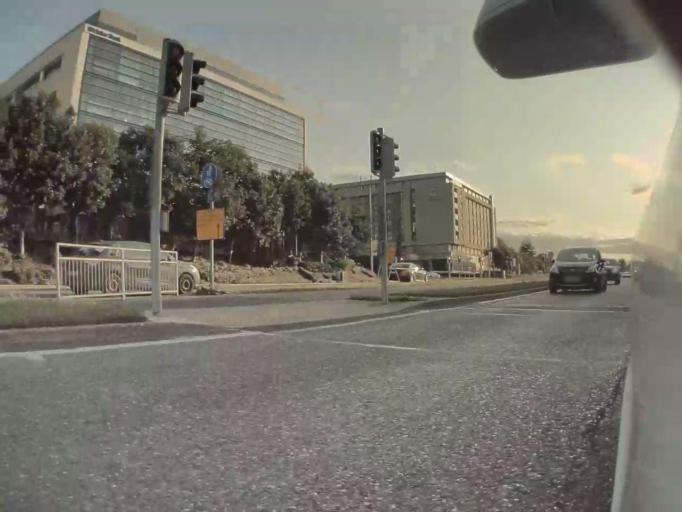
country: IE
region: Leinster
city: Sandyford
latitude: 53.2719
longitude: -6.2046
